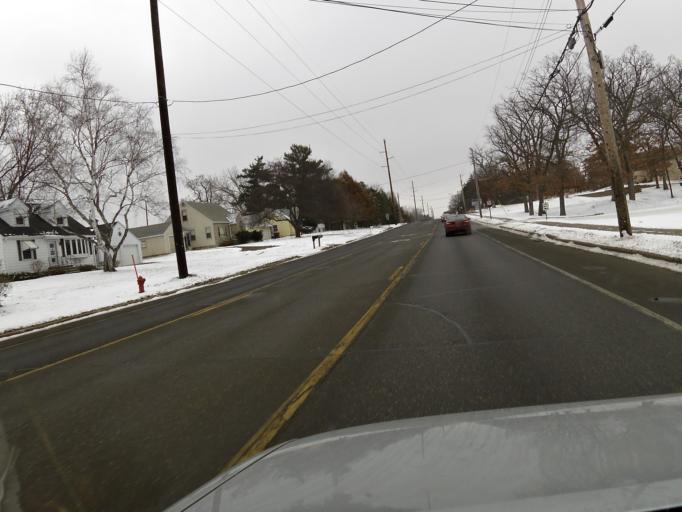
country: US
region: Minnesota
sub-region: Washington County
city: Oakdale
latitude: 44.9632
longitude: -92.9770
